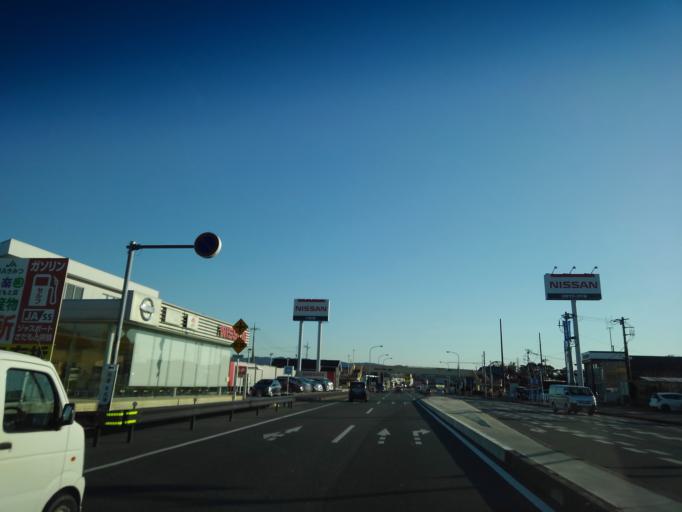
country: JP
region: Chiba
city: Kimitsu
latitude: 35.3176
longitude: 139.9267
